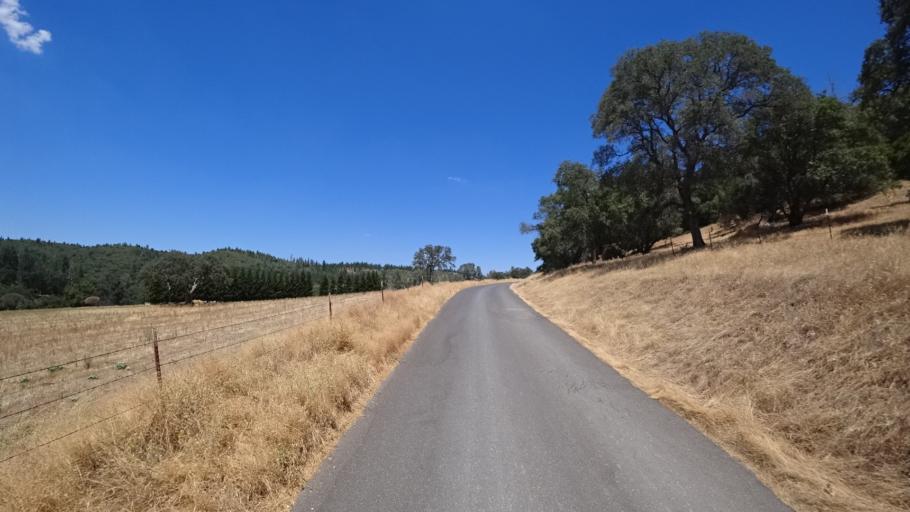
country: US
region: California
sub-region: Calaveras County
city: Murphys
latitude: 38.1137
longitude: -120.4744
